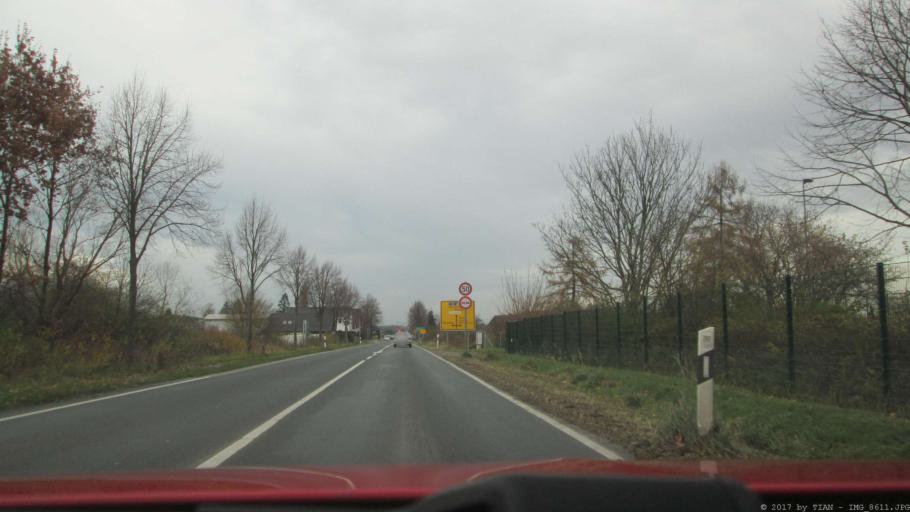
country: DE
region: Lower Saxony
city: Danndorf
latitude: 52.4163
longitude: 10.8480
